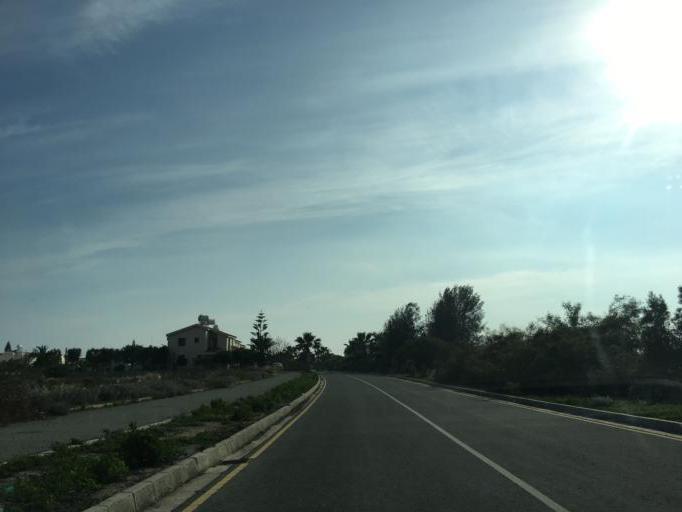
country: CY
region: Larnaka
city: Tersefanou
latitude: 34.7916
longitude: 33.5014
